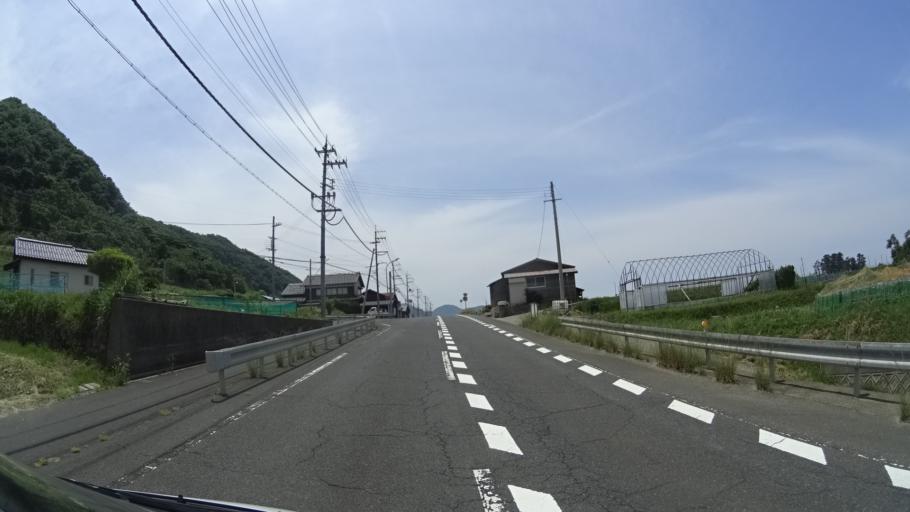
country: JP
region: Kyoto
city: Miyazu
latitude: 35.7625
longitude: 135.1904
